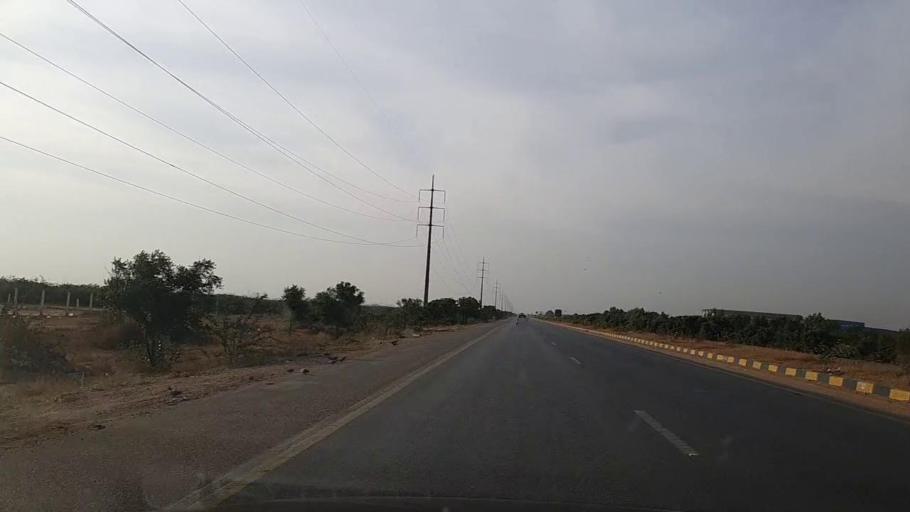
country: PK
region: Sindh
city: Gharo
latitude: 24.8261
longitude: 67.4731
